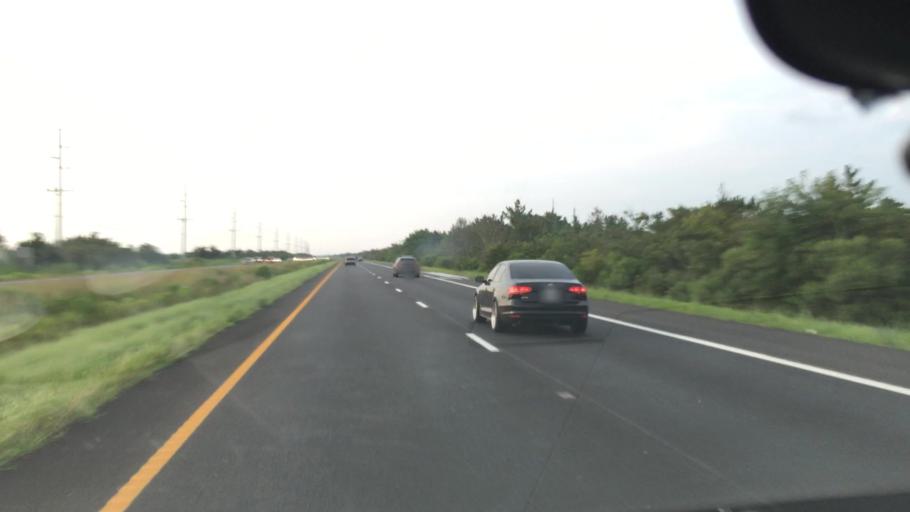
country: US
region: Delaware
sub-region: Sussex County
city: Rehoboth Beach
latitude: 38.6417
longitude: -75.0682
